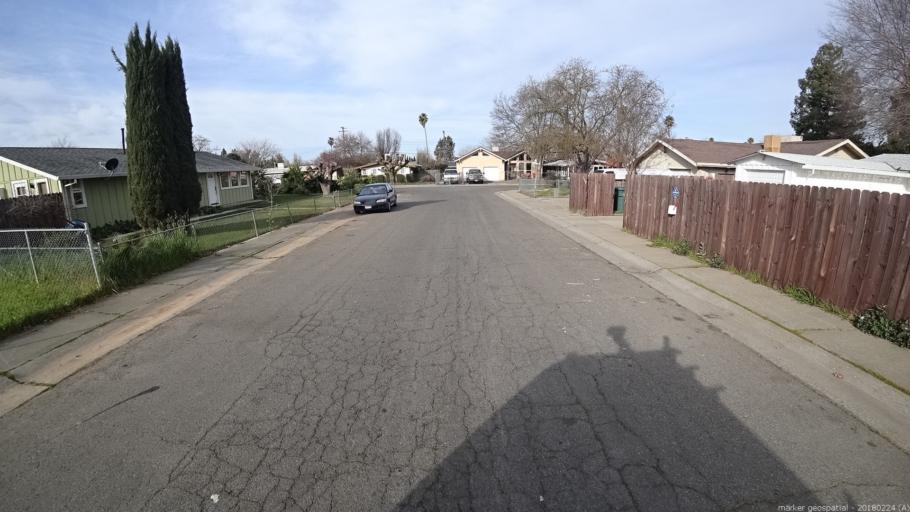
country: US
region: California
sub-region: Sacramento County
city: Rio Linda
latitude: 38.6850
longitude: -121.4630
